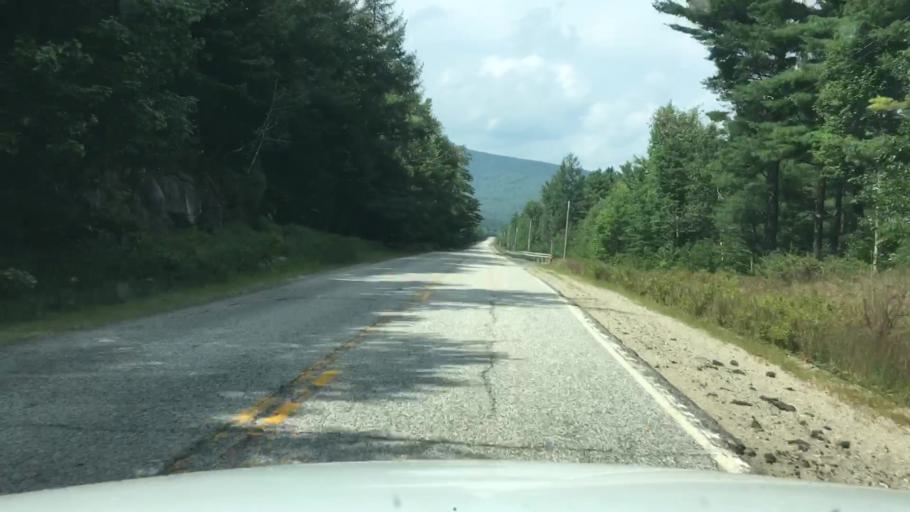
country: US
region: Maine
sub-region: Oxford County
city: Rumford
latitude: 44.5693
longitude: -70.7179
